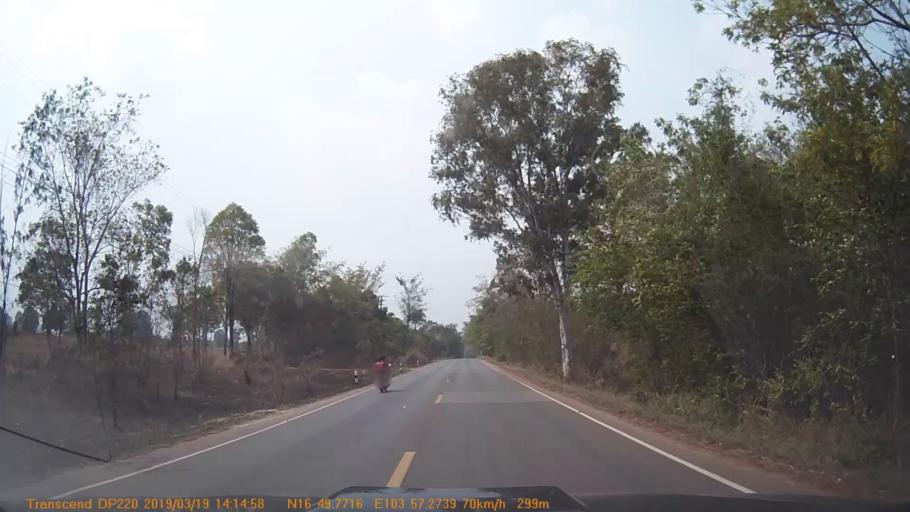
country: TH
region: Kalasin
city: Na Khu
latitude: 16.8299
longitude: 103.9542
